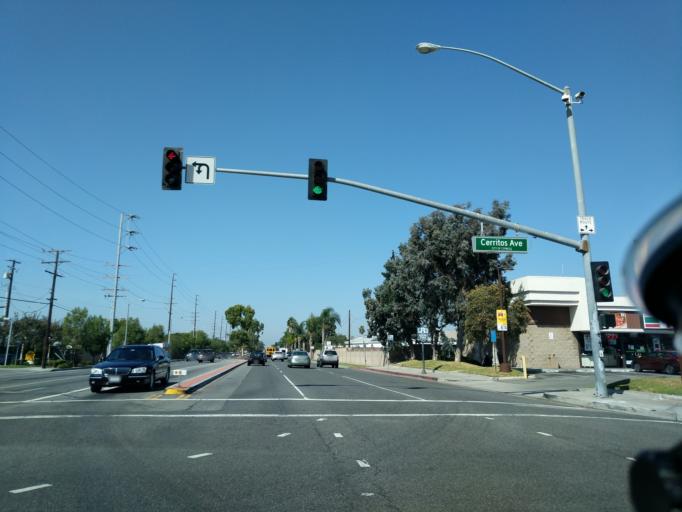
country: US
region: California
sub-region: Orange County
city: Cypress
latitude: 33.8099
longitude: -118.0281
